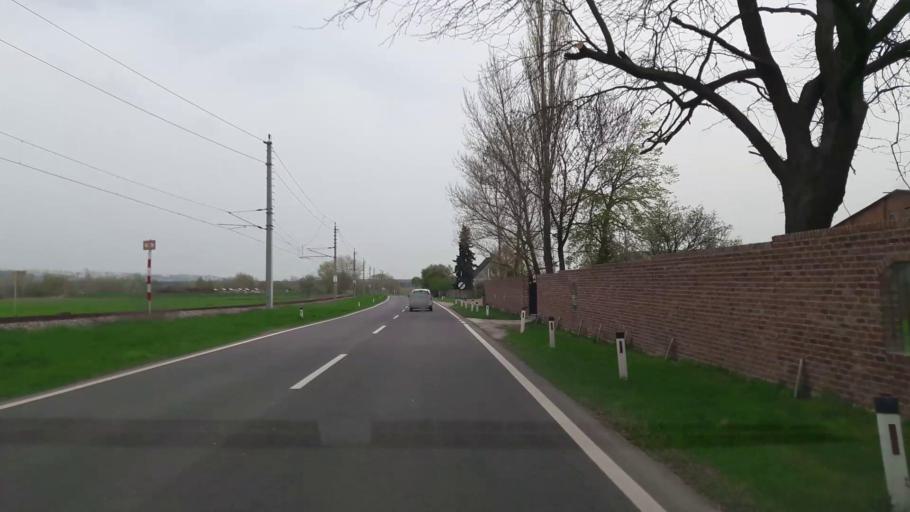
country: AT
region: Lower Austria
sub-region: Politischer Bezirk Bruck an der Leitha
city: Wolfsthal
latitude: 48.1438
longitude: 16.9763
